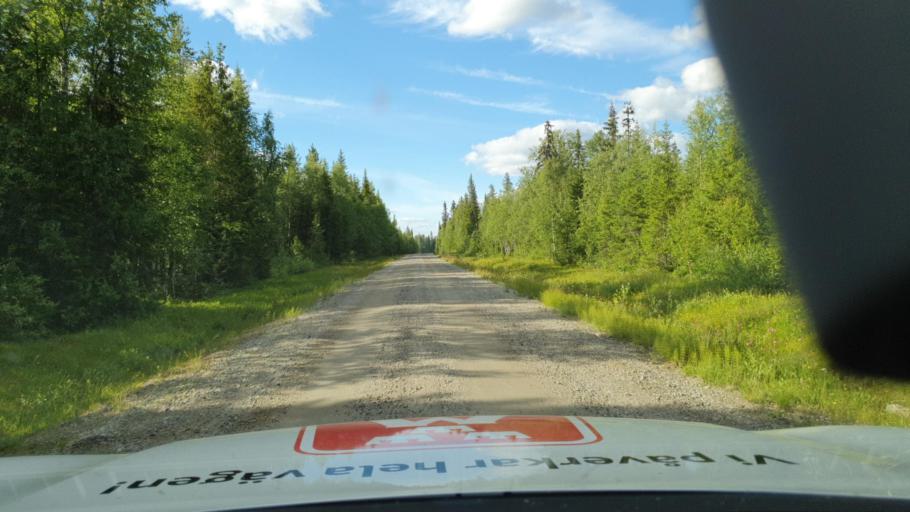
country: SE
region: Vaesterbotten
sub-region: Lycksele Kommun
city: Lycksele
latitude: 64.4365
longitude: 18.2711
